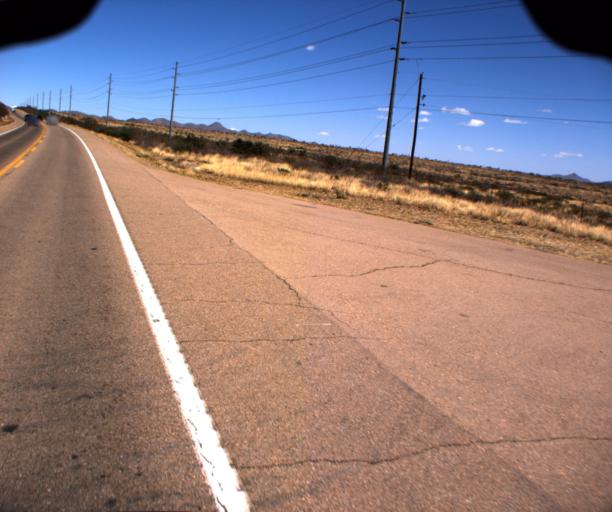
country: US
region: Arizona
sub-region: Cochise County
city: Naco
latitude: 31.3740
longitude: -109.9732
